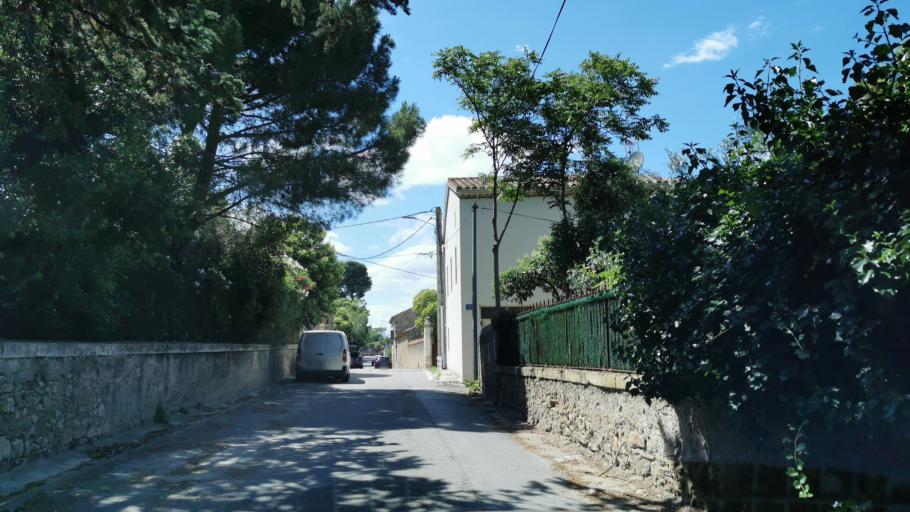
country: FR
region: Languedoc-Roussillon
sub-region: Departement de l'Aude
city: Saint-Marcel-sur-Aude
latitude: 43.2442
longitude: 2.9236
